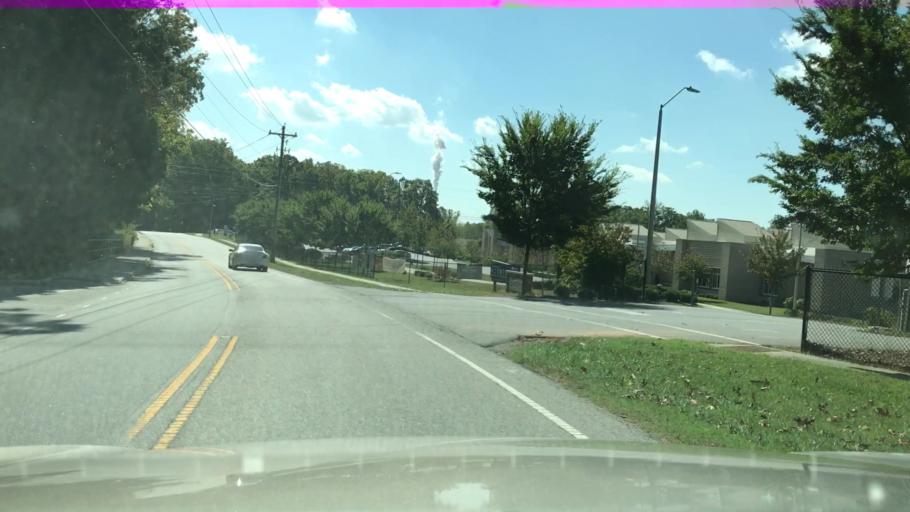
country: US
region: North Carolina
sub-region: Buncombe County
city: Royal Pines
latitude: 35.4850
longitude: -82.5386
